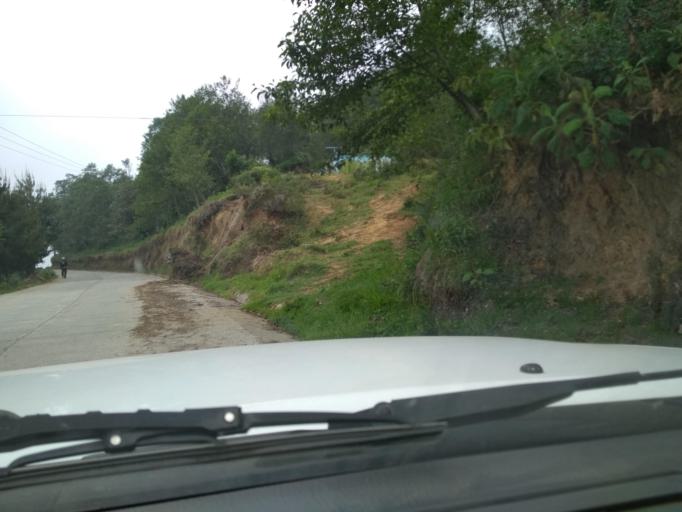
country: MX
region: Veracruz
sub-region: La Perla
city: Chilapa
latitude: 18.9896
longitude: -97.1572
